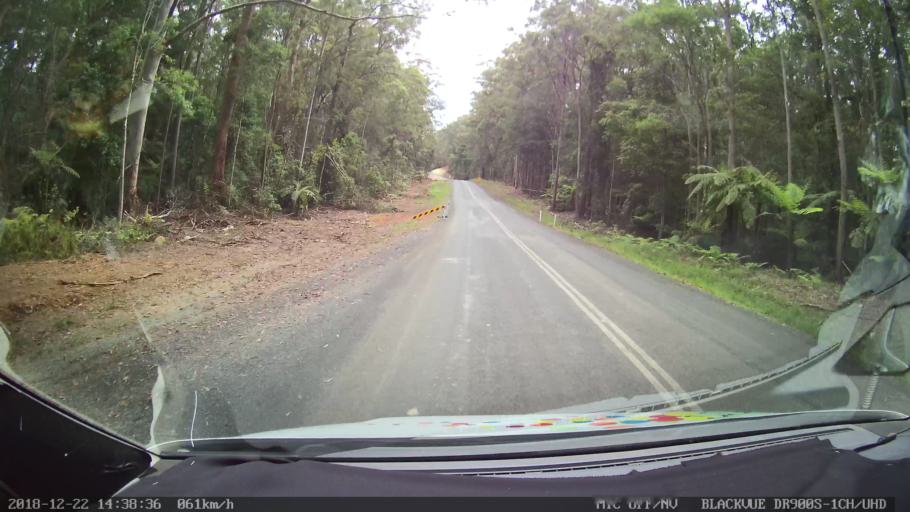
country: AU
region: New South Wales
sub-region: Bellingen
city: Dorrigo
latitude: -30.1395
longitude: 152.5966
